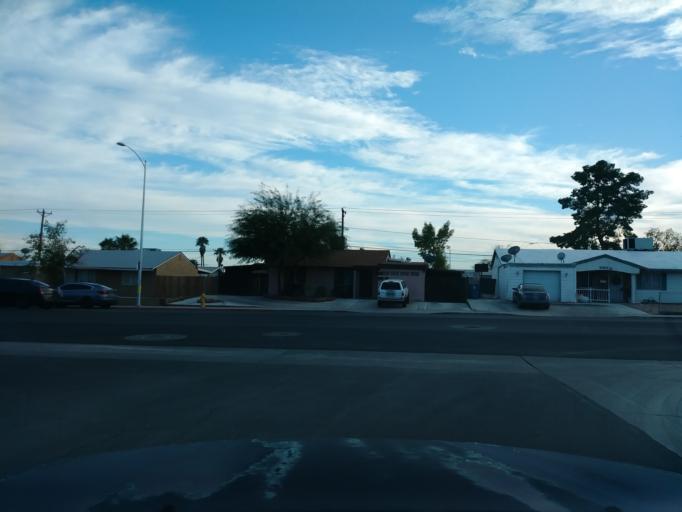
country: US
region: Nevada
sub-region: Clark County
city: Spring Valley
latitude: 36.1666
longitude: -115.2404
